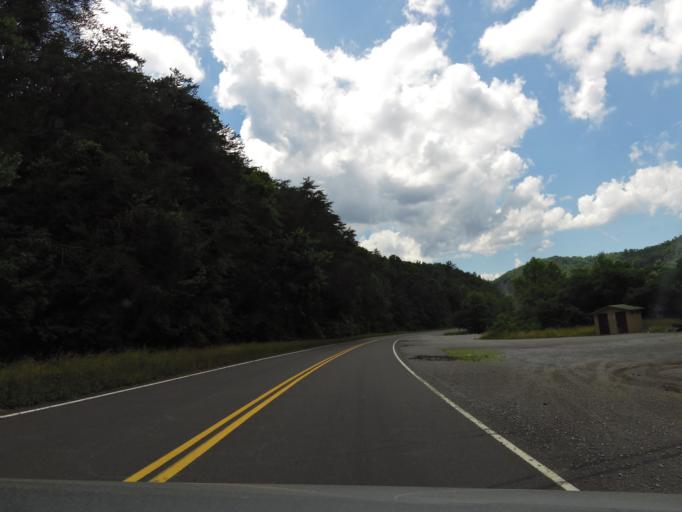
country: US
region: Tennessee
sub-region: Blount County
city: Maryville
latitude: 35.5468
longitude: -83.9915
